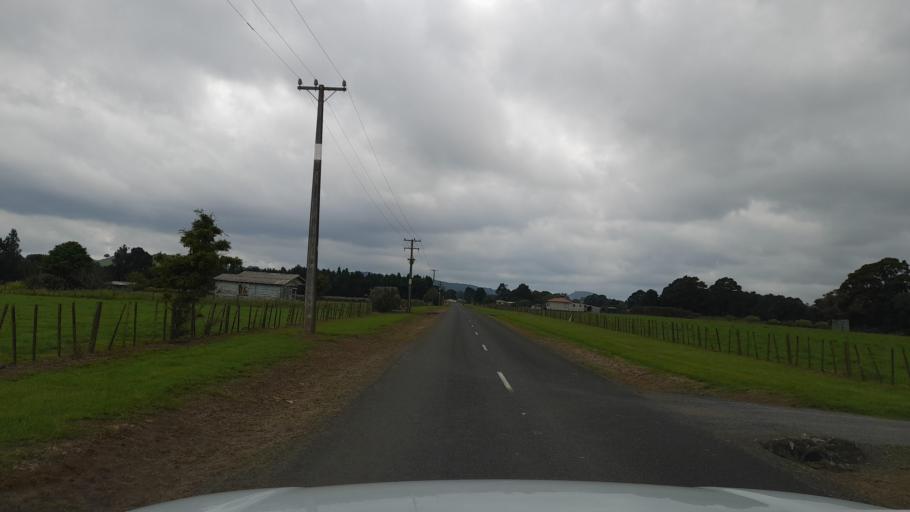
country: NZ
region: Northland
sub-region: Far North District
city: Waimate North
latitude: -35.4286
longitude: 173.7937
